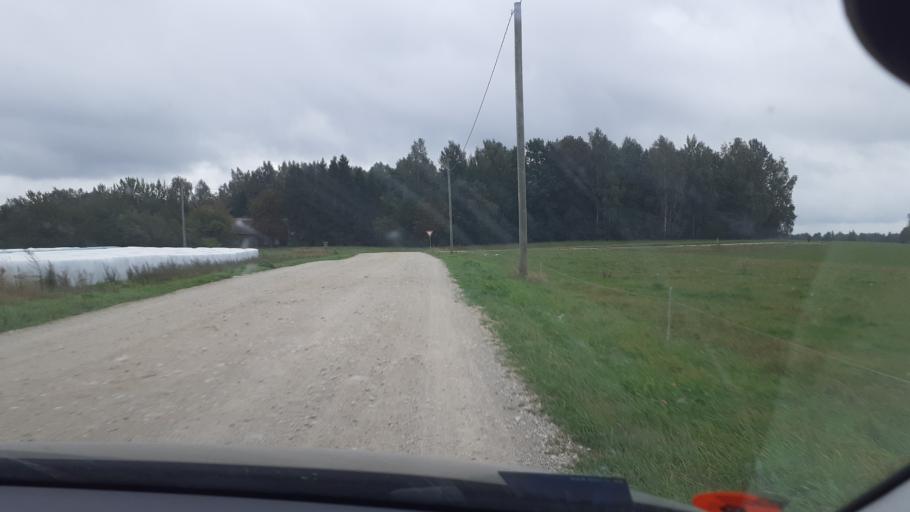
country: LV
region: Alsunga
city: Alsunga
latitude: 56.8961
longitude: 21.6895
